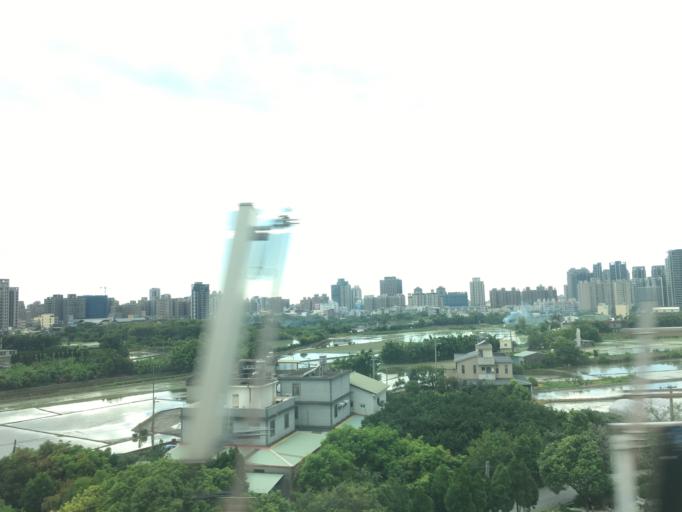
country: TW
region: Taiwan
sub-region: Hsinchu
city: Zhubei
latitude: 24.8162
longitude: 121.0422
